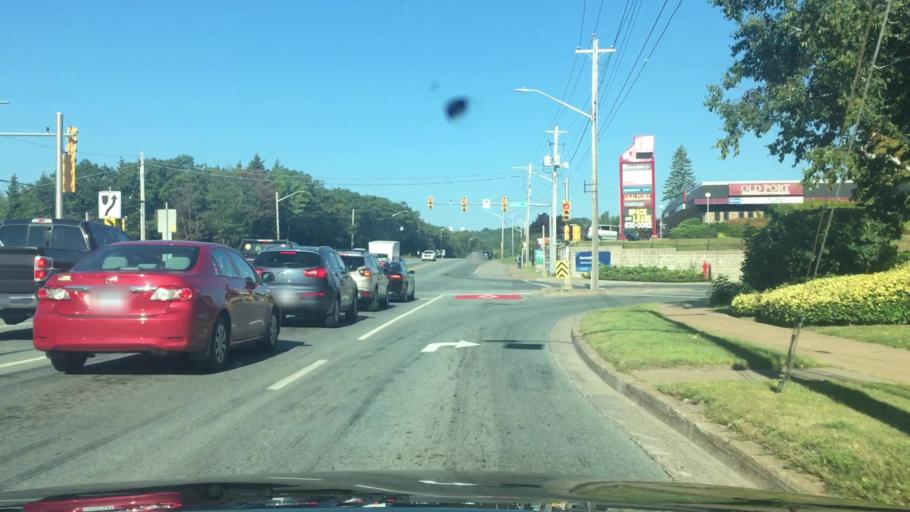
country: CA
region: Nova Scotia
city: Dartmouth
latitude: 44.7033
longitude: -63.6112
